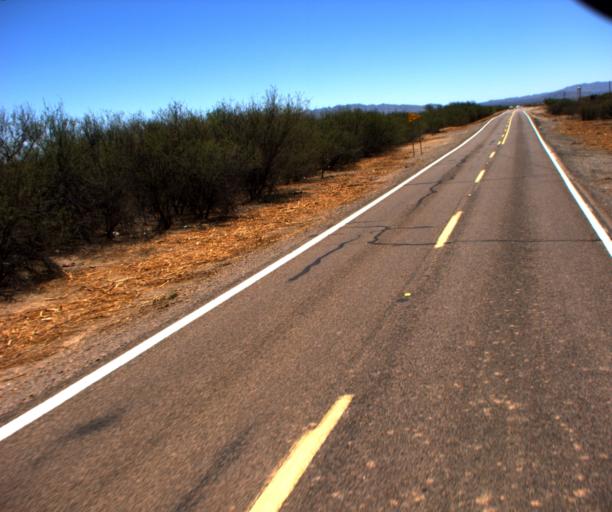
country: US
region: Arizona
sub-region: Pima County
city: Ajo
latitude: 32.1914
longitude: -112.4216
